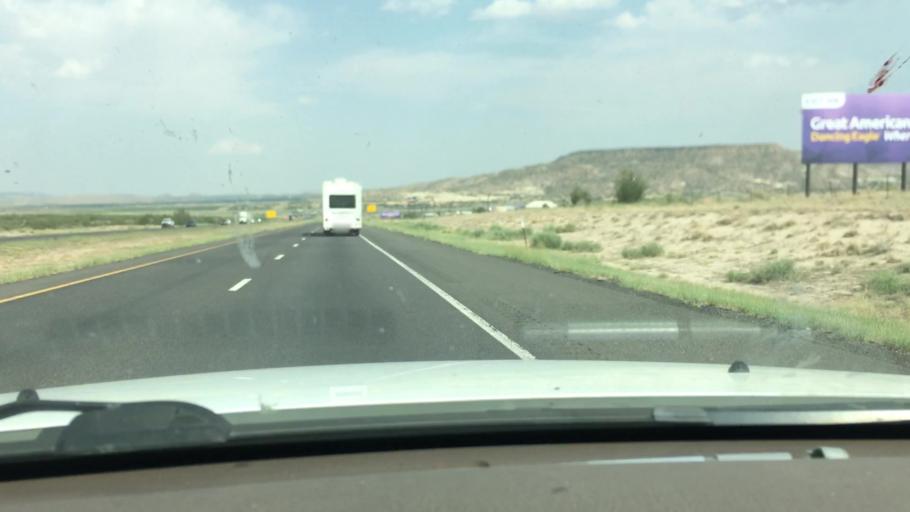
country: US
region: New Mexico
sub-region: Cibola County
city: Laguna
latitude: 35.0370
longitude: -107.4852
